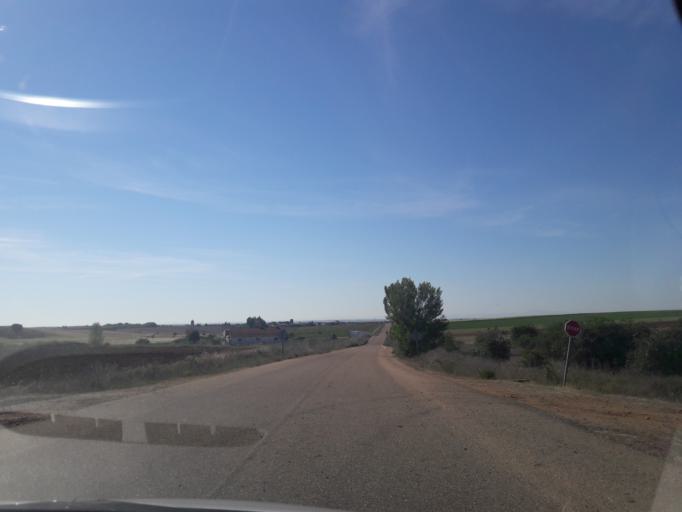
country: ES
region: Castille and Leon
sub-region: Provincia de Salamanca
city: Parada de Rubiales
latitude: 41.1567
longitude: -5.4497
